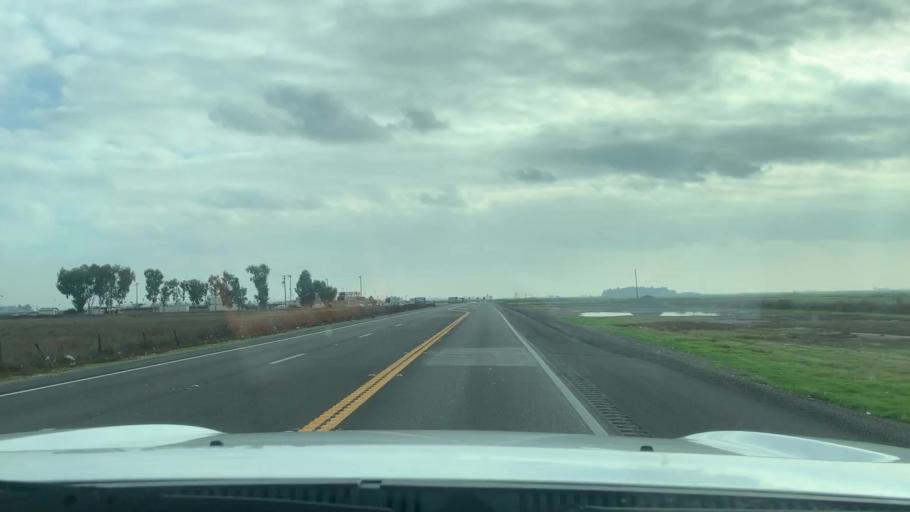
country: US
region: California
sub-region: Kings County
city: Lemoore
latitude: 36.2716
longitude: -119.8078
